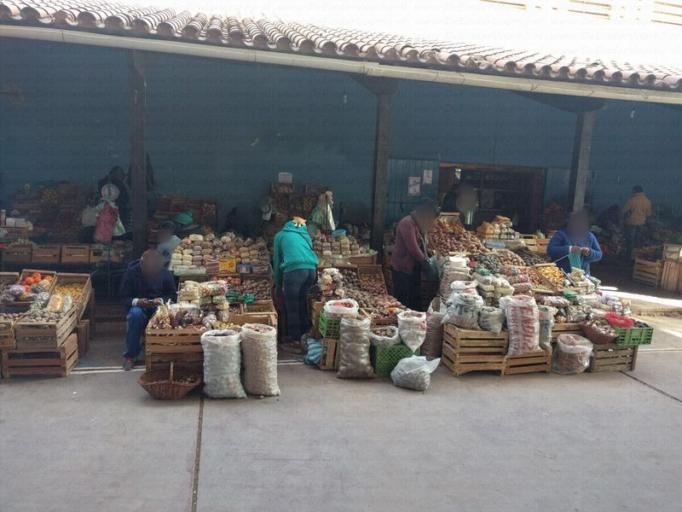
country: AR
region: Jujuy
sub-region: Departamento de Tilcara
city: Tilcara
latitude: -23.5758
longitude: -65.3944
